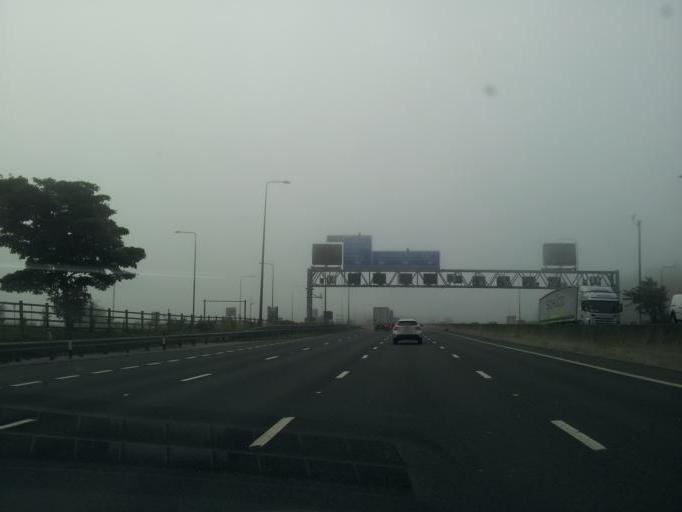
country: GB
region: England
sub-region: Kirklees
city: Cleckheaton
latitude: 53.7119
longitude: -1.7450
